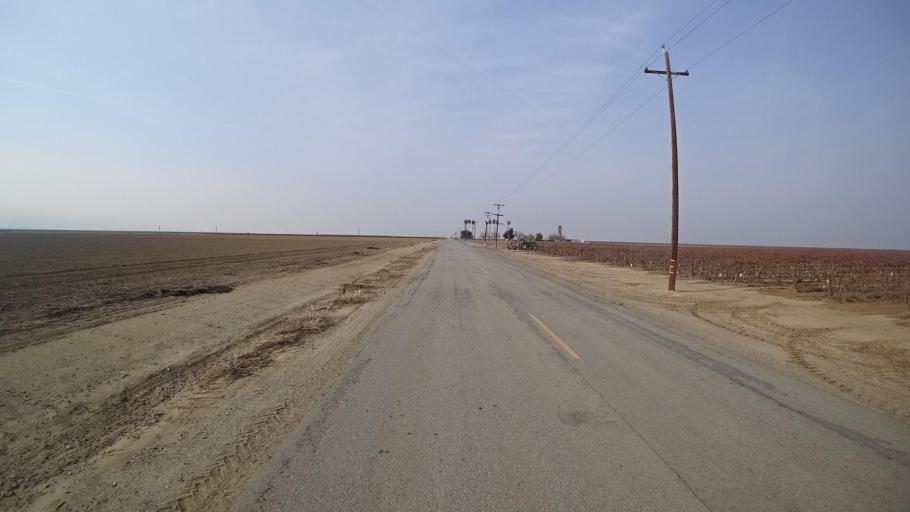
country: US
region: California
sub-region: Kern County
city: Greenfield
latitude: 35.0766
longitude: -119.0772
